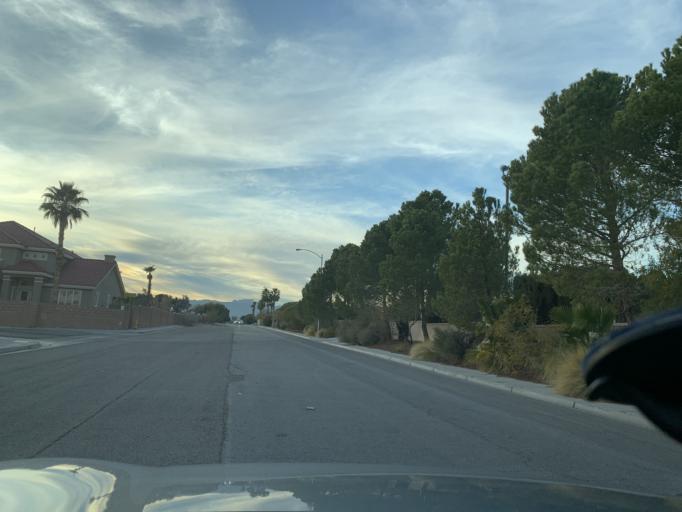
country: US
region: Nevada
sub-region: Clark County
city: Spring Valley
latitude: 36.0908
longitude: -115.2276
